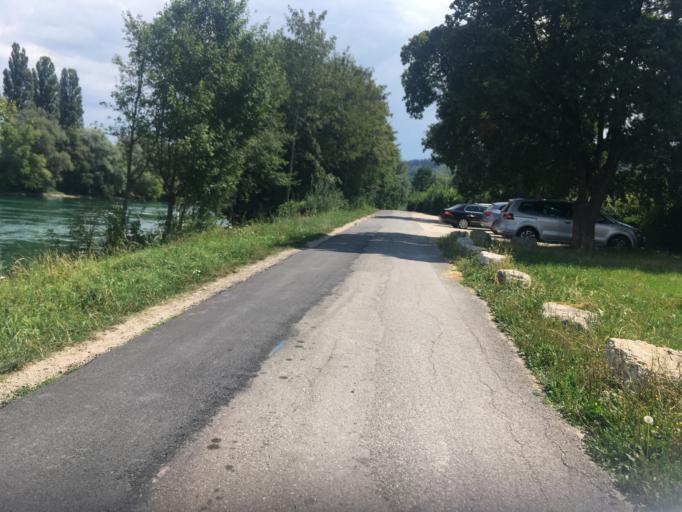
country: CH
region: Bern
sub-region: Biel/Bienne District
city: Bellmund
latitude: 47.1177
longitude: 7.2588
